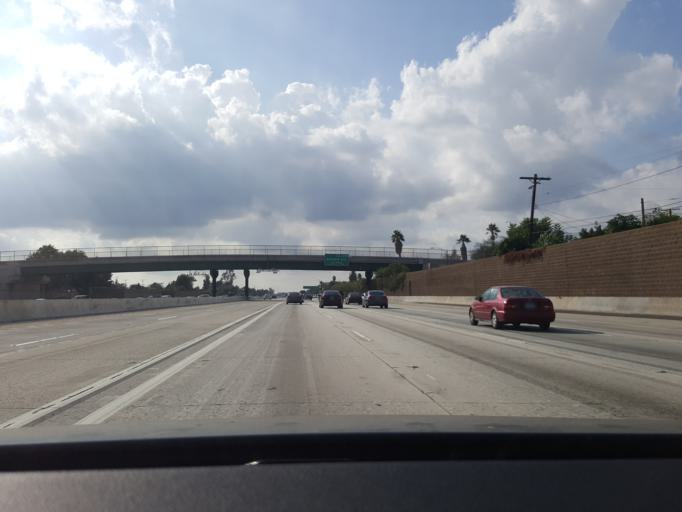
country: US
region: California
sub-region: Los Angeles County
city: Monterey Park
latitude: 34.0719
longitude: -118.1161
